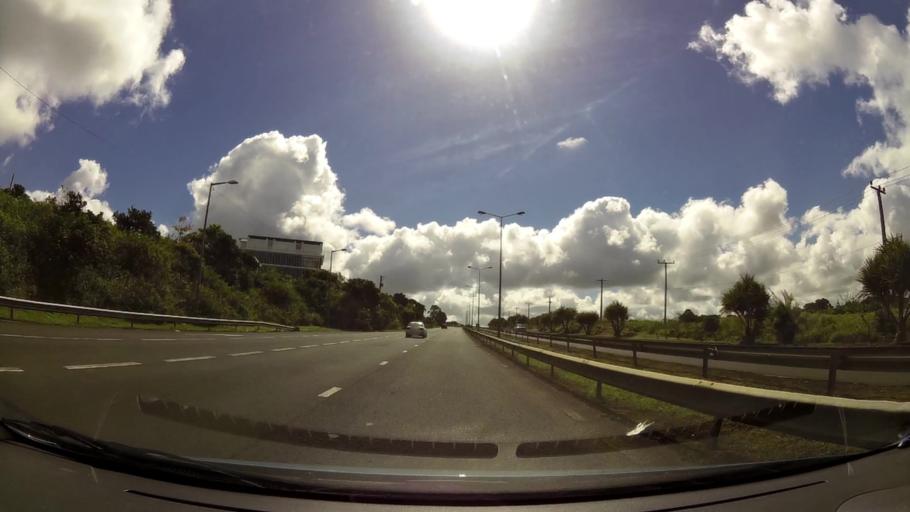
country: MU
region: Grand Port
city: Nouvelle France
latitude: -20.3879
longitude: 57.5735
